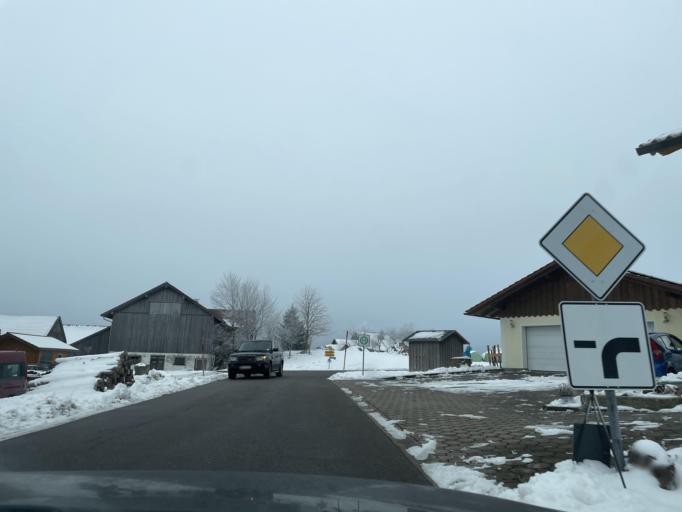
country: DE
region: Bavaria
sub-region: Lower Bavaria
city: Achslach
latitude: 49.0129
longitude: 12.9033
